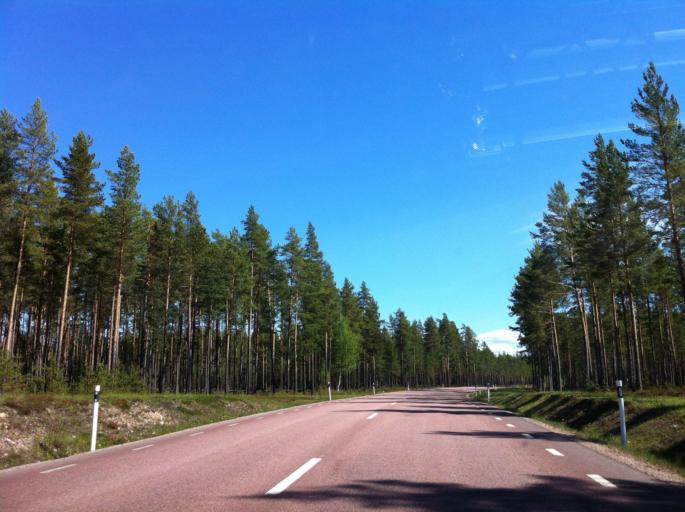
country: SE
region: Dalarna
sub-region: Mora Kommun
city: Mora
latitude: 60.9617
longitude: 14.6944
